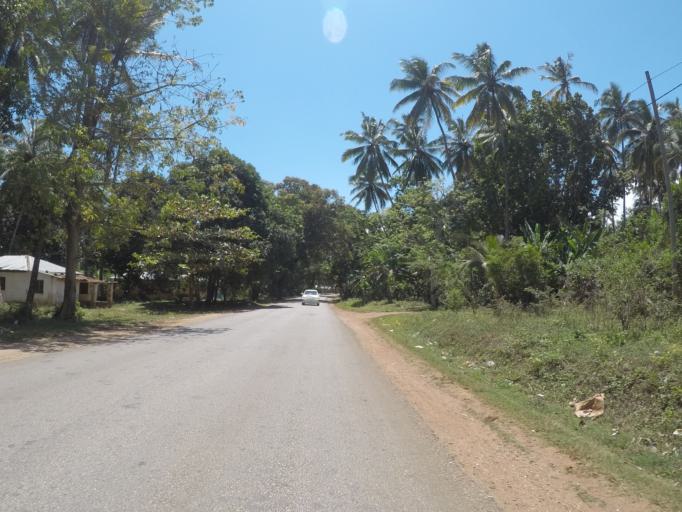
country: TZ
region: Zanzibar Central/South
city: Koani
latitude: -6.2147
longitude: 39.3239
